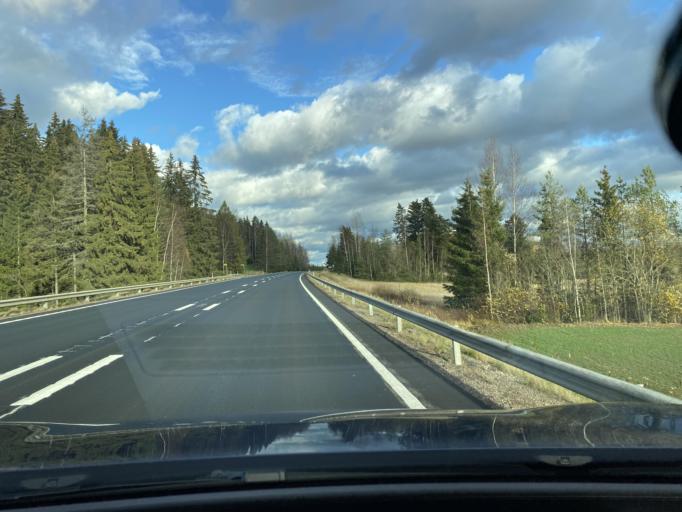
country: FI
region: Haeme
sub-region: Riihimaeki
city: Oitti
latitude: 60.8356
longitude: 25.0913
